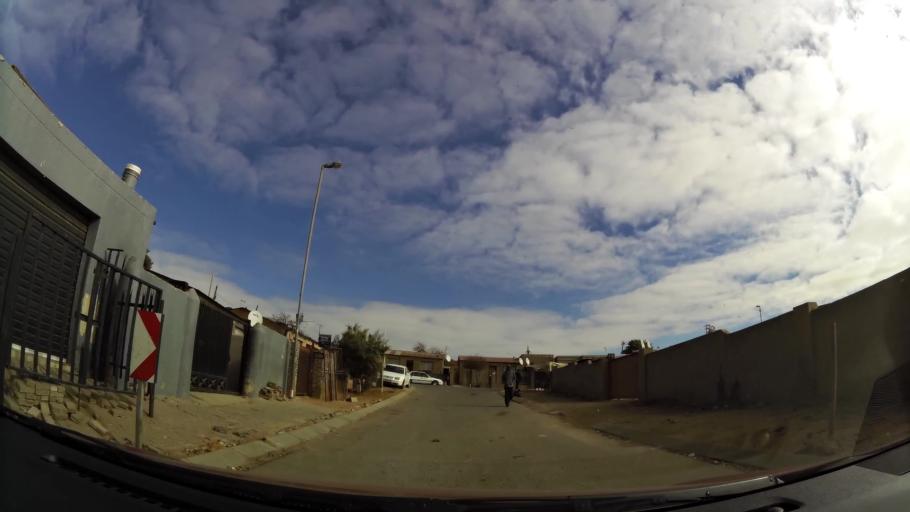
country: ZA
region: Gauteng
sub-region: City of Johannesburg Metropolitan Municipality
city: Modderfontein
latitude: -26.0529
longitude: 28.1812
